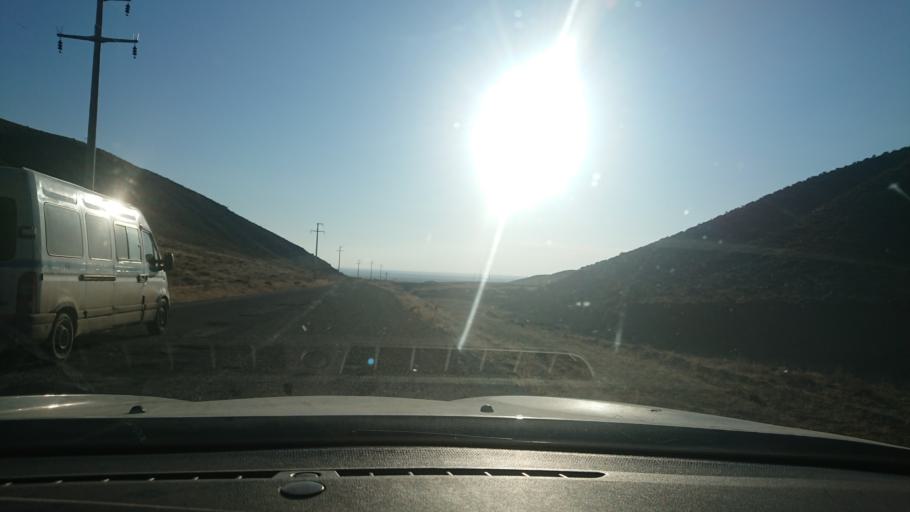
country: TR
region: Aksaray
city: Acipinar
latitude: 38.6873
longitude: 33.7417
